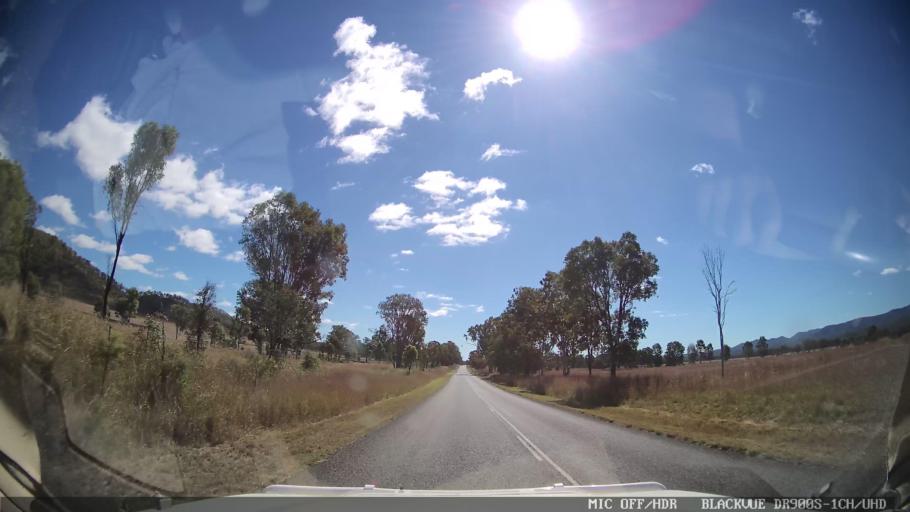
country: AU
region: Queensland
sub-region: Gladstone
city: Toolooa
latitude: -24.4487
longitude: 151.3443
